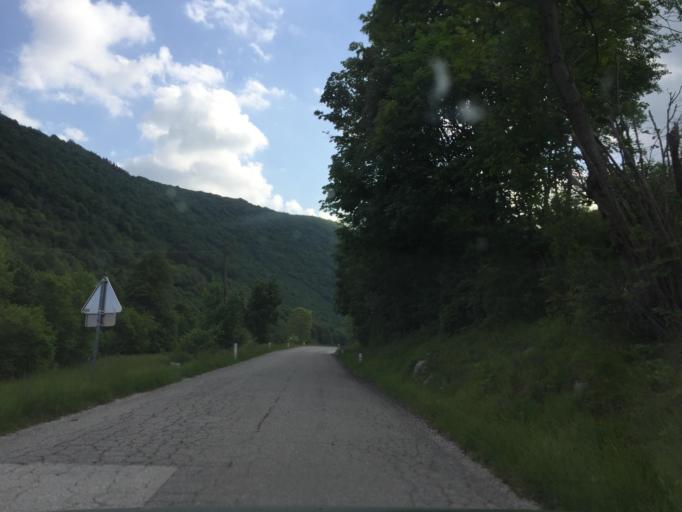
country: SI
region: Nova Gorica
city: Sempas
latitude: 46.0155
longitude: 13.7390
